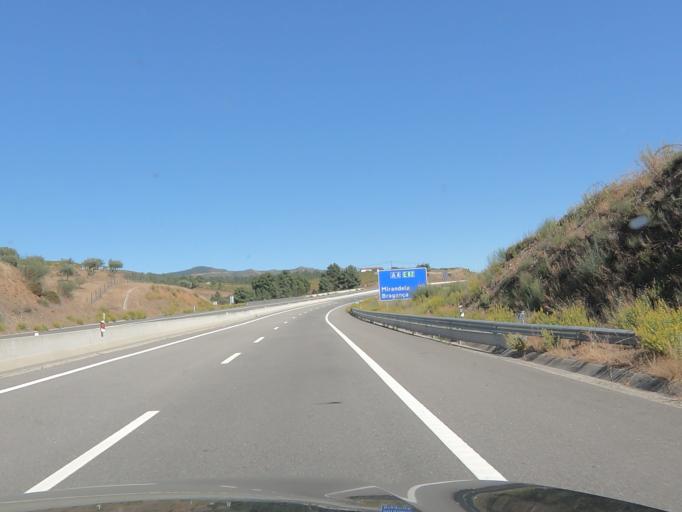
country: PT
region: Vila Real
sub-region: Murca
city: Murca
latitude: 41.4010
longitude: -7.4415
